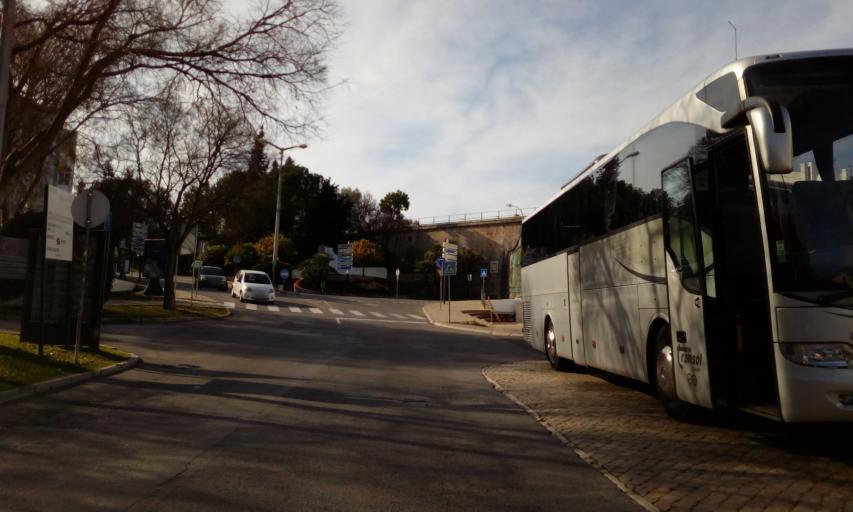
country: PT
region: Faro
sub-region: Tavira
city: Tavira
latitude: 37.1250
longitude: -7.6546
